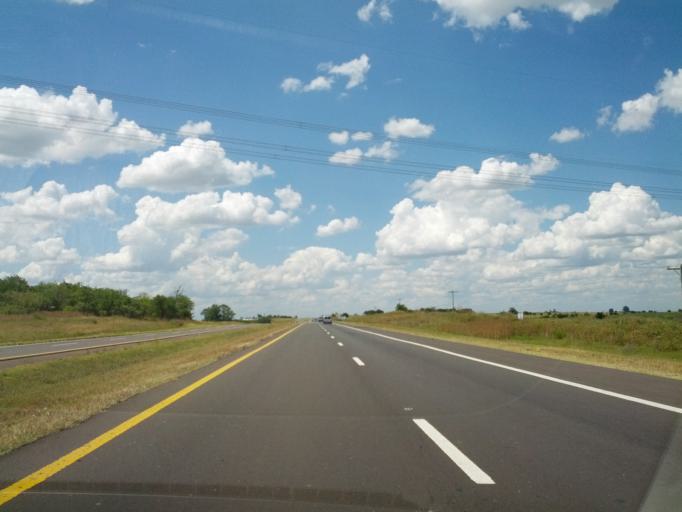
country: AR
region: Entre Rios
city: Colonia Elia
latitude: -32.5678
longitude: -58.3760
